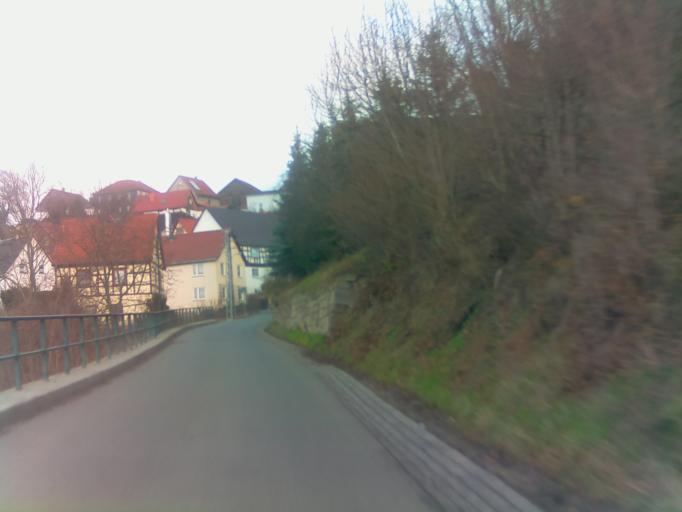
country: DE
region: Thuringia
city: Rudolstadt
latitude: 50.6913
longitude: 11.3388
